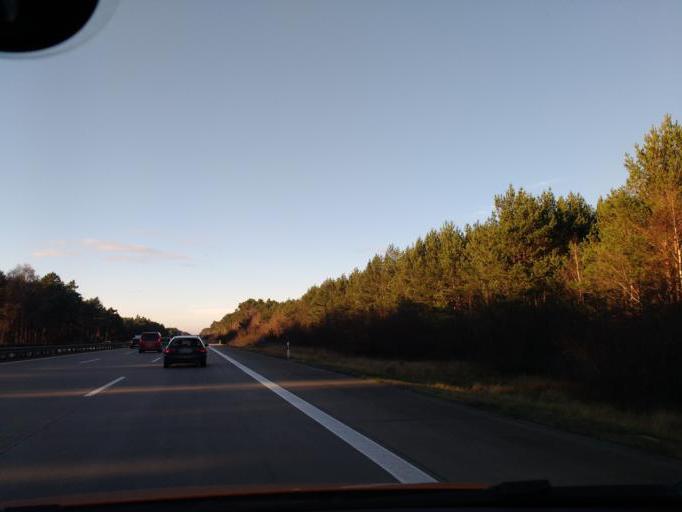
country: DE
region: Brandenburg
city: Wenzlow
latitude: 52.2766
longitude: 12.4256
